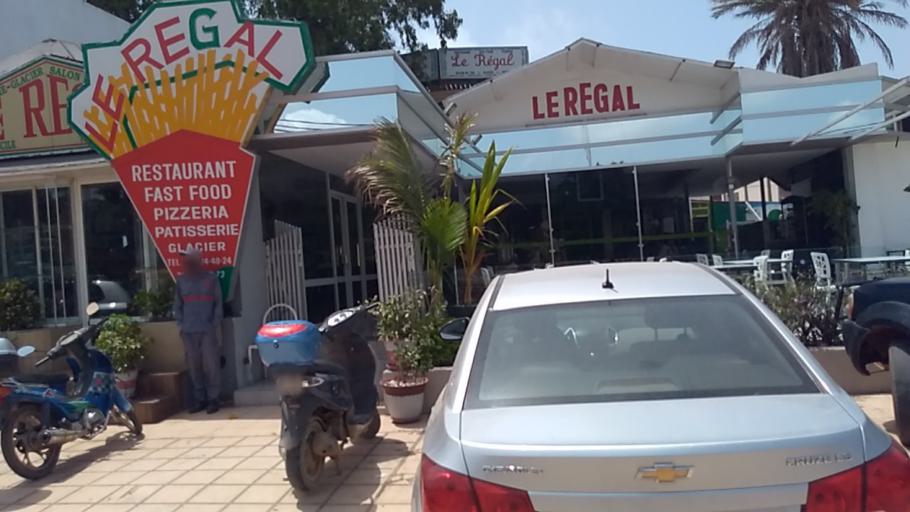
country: SN
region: Dakar
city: Mermoz Boabab
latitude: 14.7178
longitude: -17.4867
